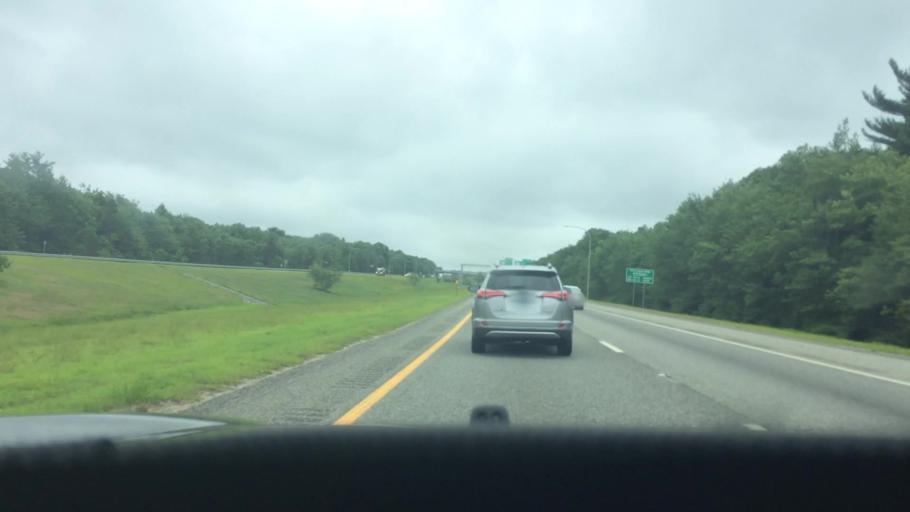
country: US
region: Rhode Island
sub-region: Kent County
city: West Greenwich
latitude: 41.6104
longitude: -71.6546
